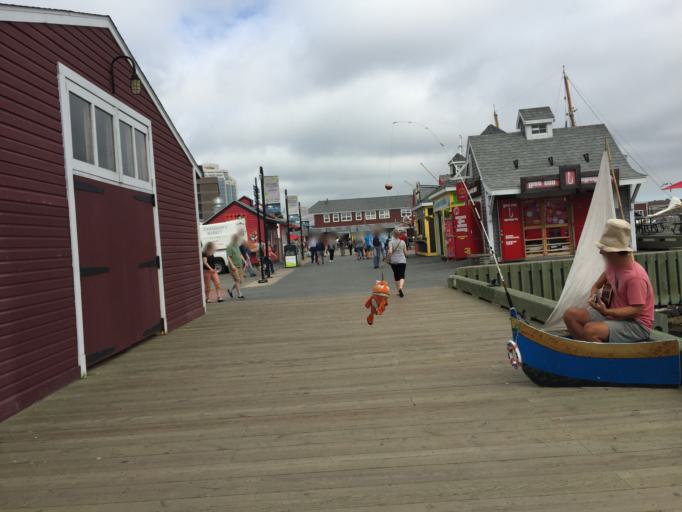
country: CA
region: Nova Scotia
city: Halifax
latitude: 44.6480
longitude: -63.5705
